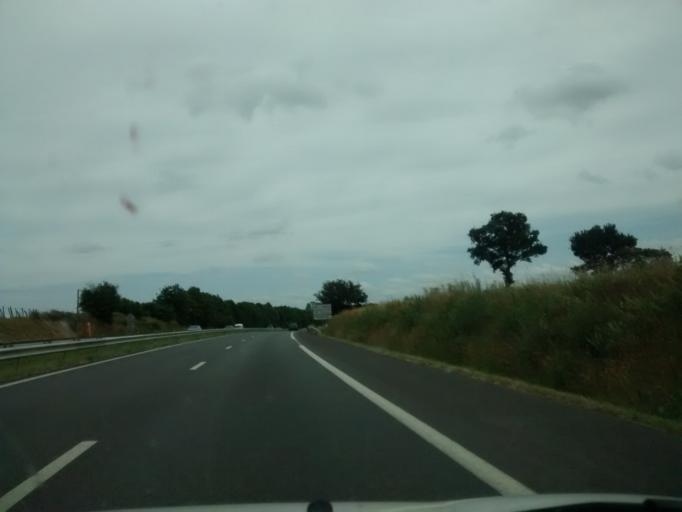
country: FR
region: Brittany
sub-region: Departement des Cotes-d'Armor
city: Sevignac
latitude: 48.3523
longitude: -2.2964
